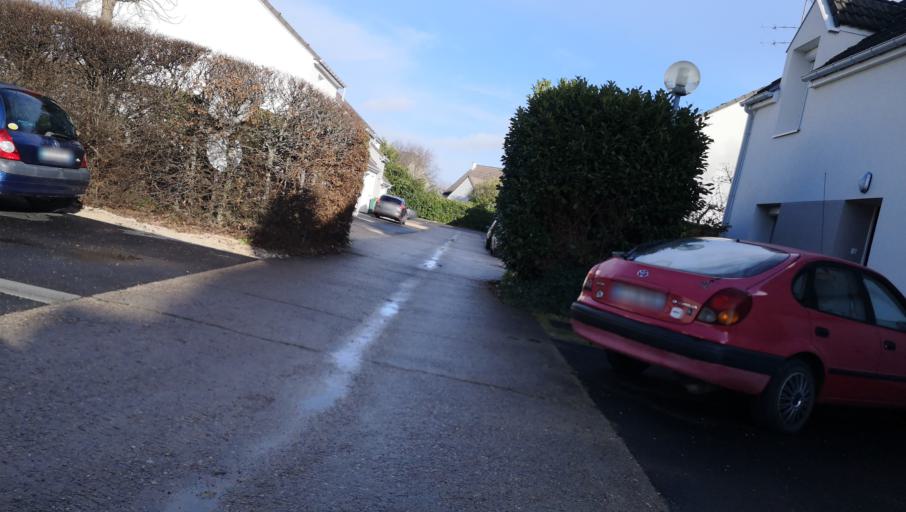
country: FR
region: Centre
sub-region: Departement du Loiret
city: Saint-Pryve-Saint-Mesmin
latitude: 47.8754
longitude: 1.8693
